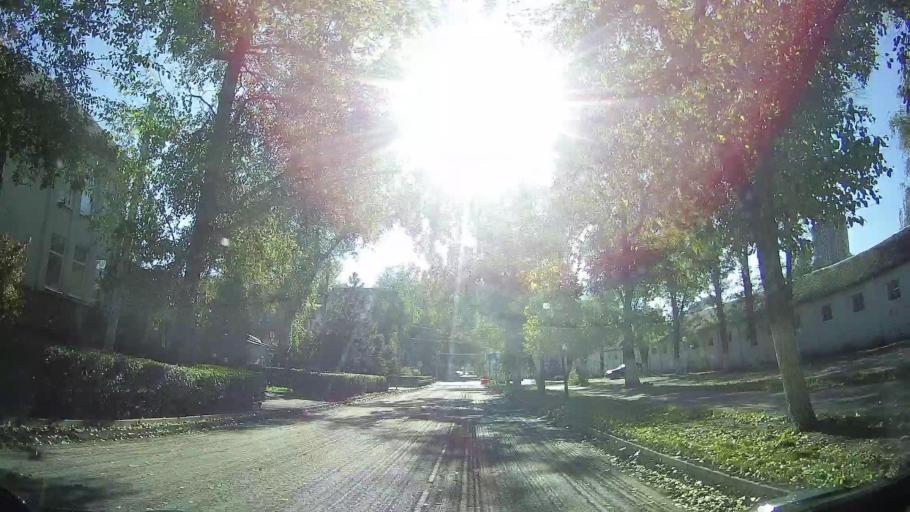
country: RU
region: Rostov
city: Rostov-na-Donu
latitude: 47.2367
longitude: 39.7297
